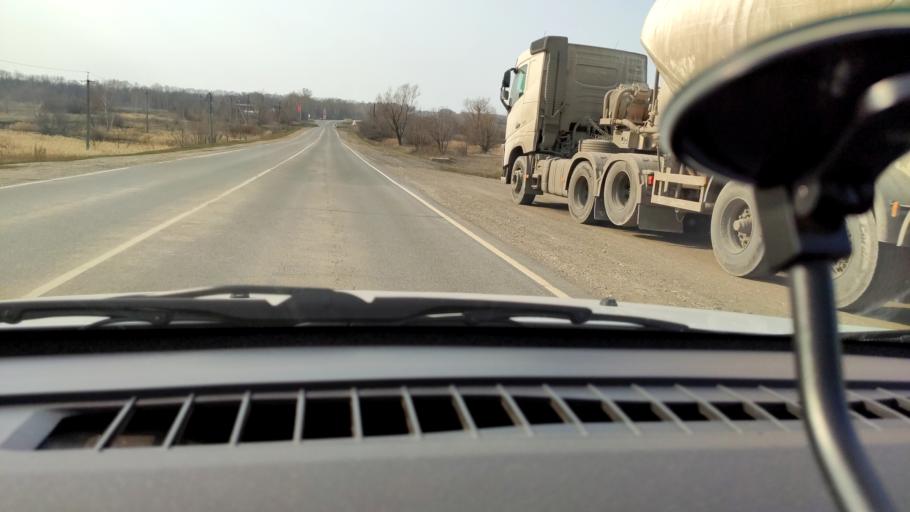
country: RU
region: Samara
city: Dubovyy Umet
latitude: 53.0635
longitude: 50.3743
